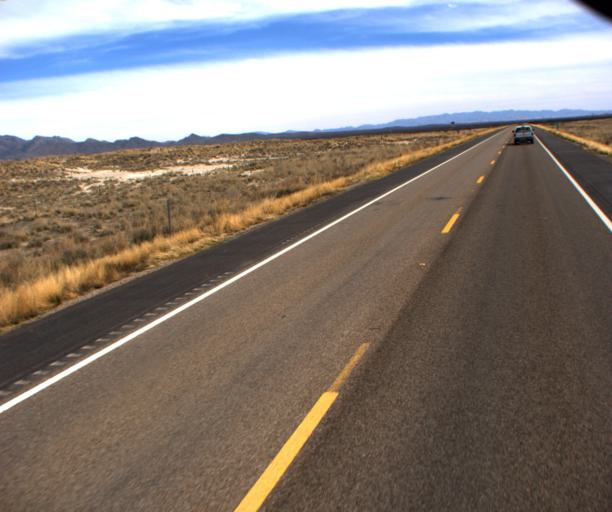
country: US
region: Arizona
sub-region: Cochise County
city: Willcox
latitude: 32.2066
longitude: -109.7732
